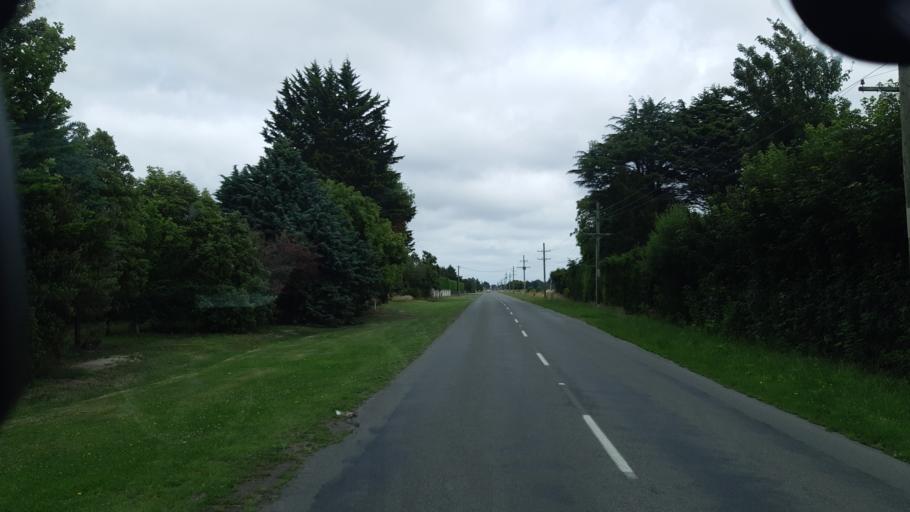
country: NZ
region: Canterbury
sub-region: Selwyn District
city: Prebbleton
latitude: -43.5079
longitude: 172.5235
